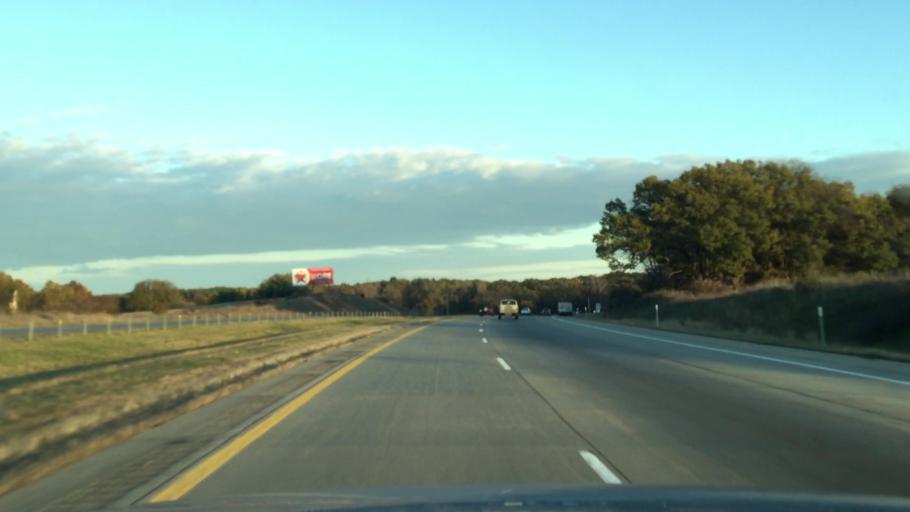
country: US
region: Michigan
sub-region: Calhoun County
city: Albion
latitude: 42.2831
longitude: -84.7956
